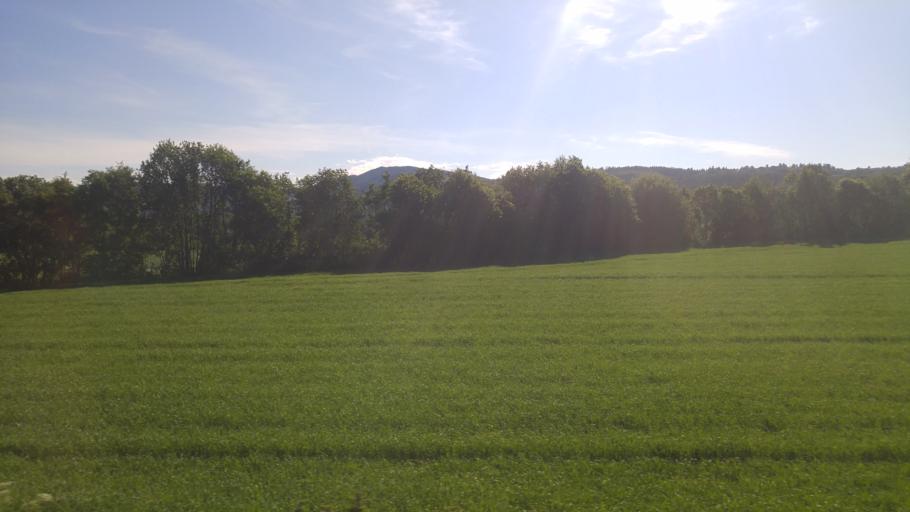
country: NO
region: Sor-Trondelag
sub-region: Melhus
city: Melhus
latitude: 63.2754
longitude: 10.2885
